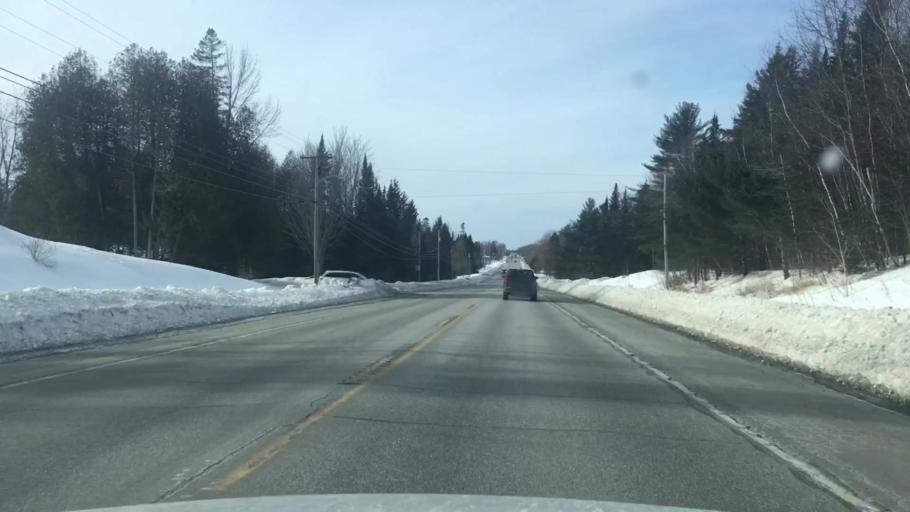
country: US
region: Maine
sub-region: Penobscot County
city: Kenduskeag
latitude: 44.9767
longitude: -68.9885
